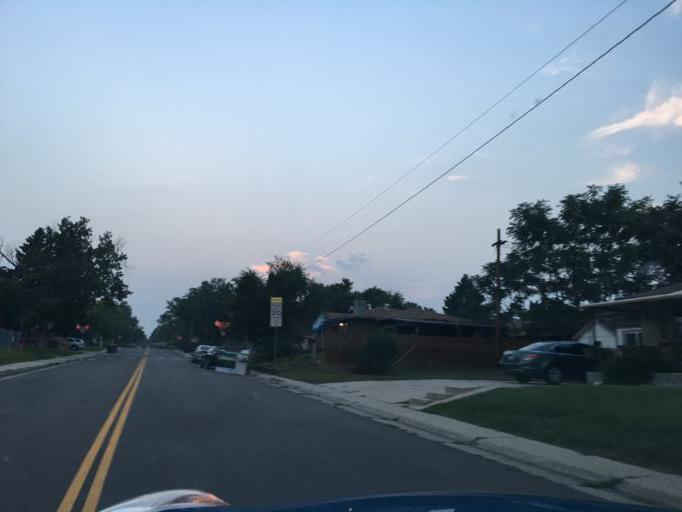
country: US
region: Colorado
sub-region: Arapahoe County
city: Sheridan
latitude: 39.6909
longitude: -105.0118
